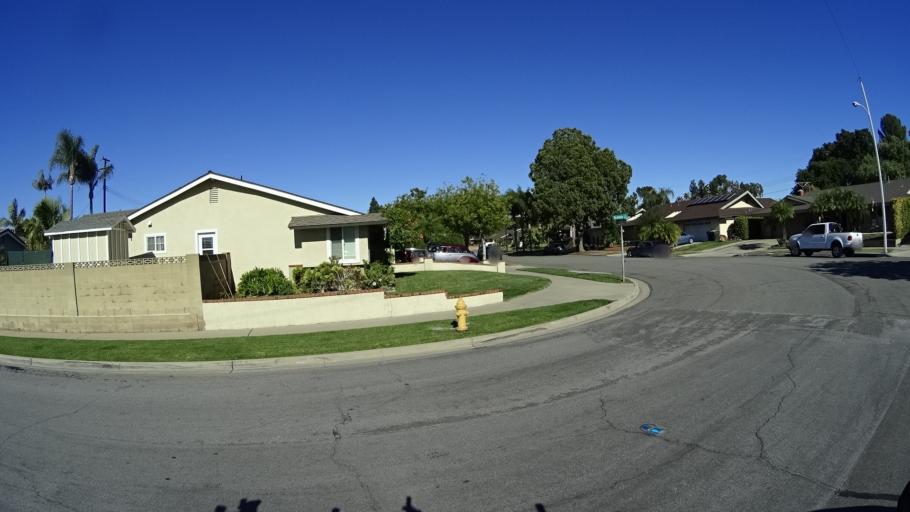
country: US
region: California
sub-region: Orange County
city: Placentia
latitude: 33.8872
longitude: -117.8469
